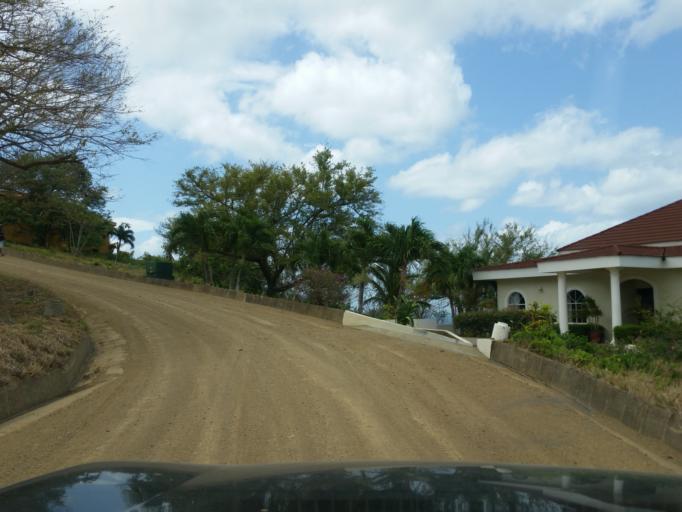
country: NI
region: Rivas
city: Tola
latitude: 11.4341
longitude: -86.0807
